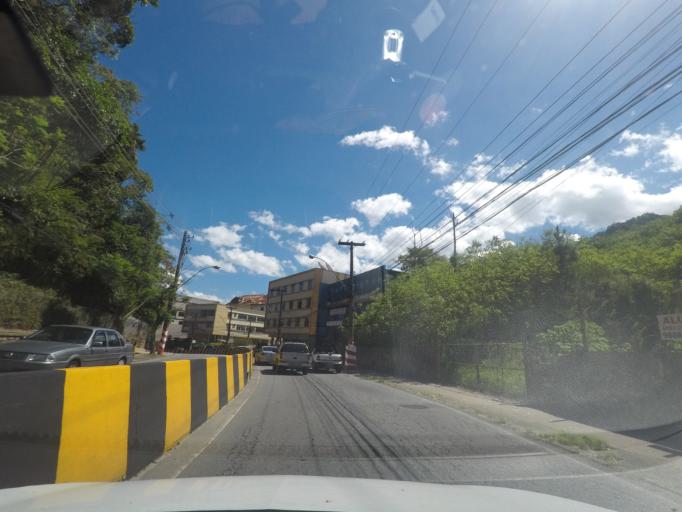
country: BR
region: Rio de Janeiro
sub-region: Teresopolis
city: Teresopolis
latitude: -22.4273
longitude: -42.9808
